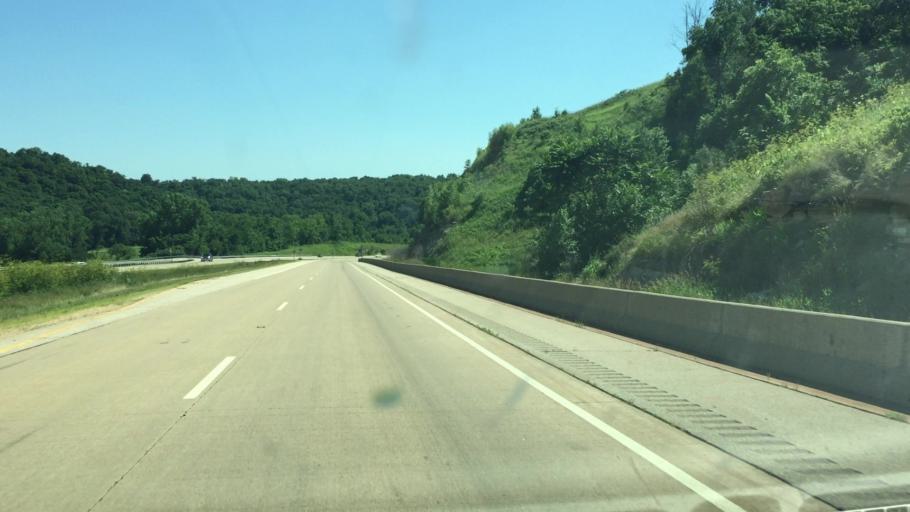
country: US
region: Wisconsin
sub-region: Grant County
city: Dickeyville
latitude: 42.6671
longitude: -90.5507
